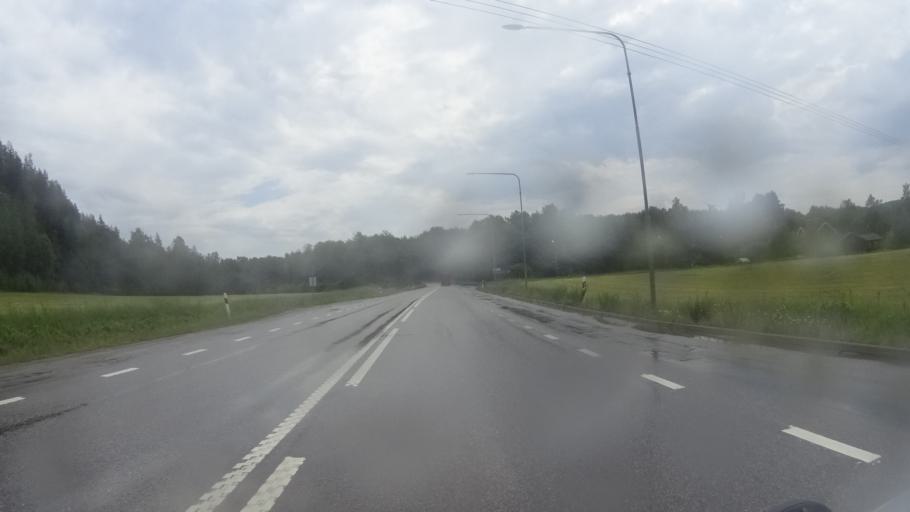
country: SE
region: OEstergoetland
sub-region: Kinda Kommun
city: Kisa
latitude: 57.9774
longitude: 15.6425
